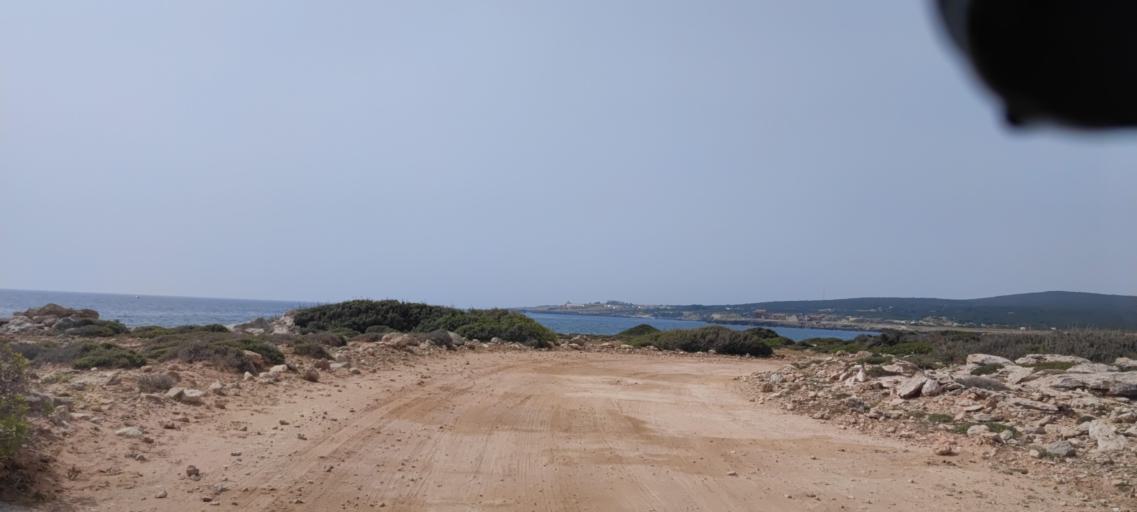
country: CY
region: Ammochostos
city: Rizokarpaso
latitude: 35.6735
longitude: 34.5776
